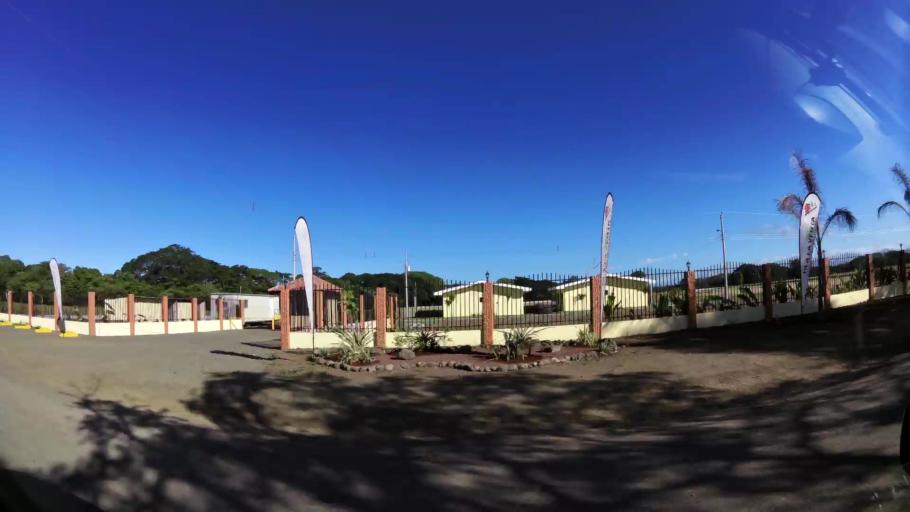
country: CR
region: Guanacaste
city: Sardinal
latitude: 10.4856
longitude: -85.5783
